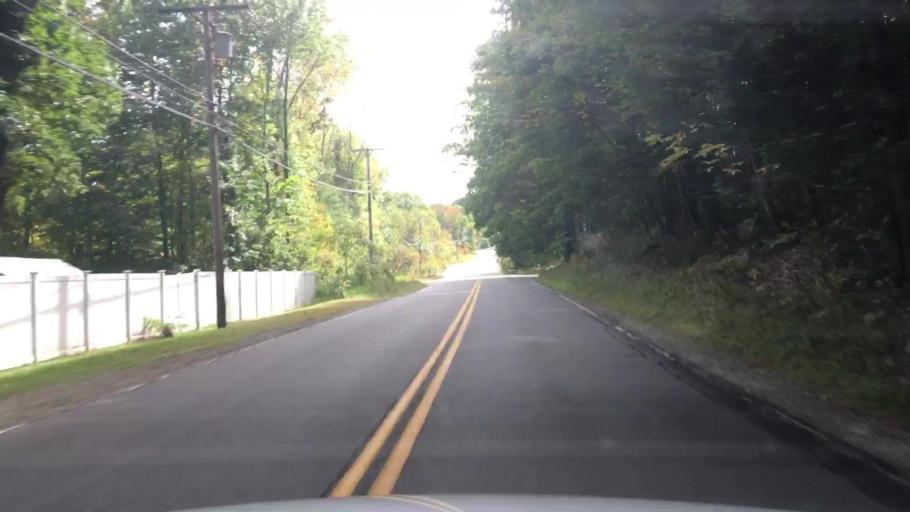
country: US
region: Maine
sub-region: Androscoggin County
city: Lewiston
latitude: 44.0389
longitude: -70.1896
